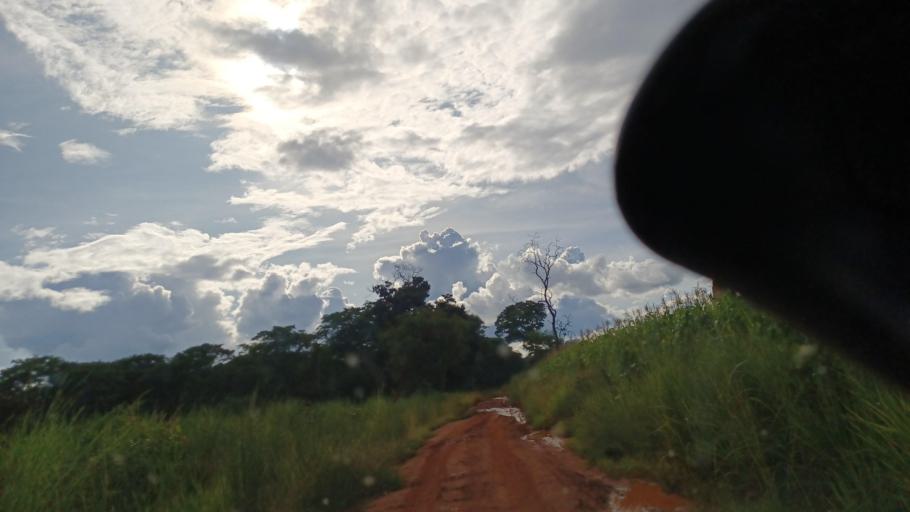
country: ZM
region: North-Western
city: Kasempa
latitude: -13.6782
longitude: 26.3107
